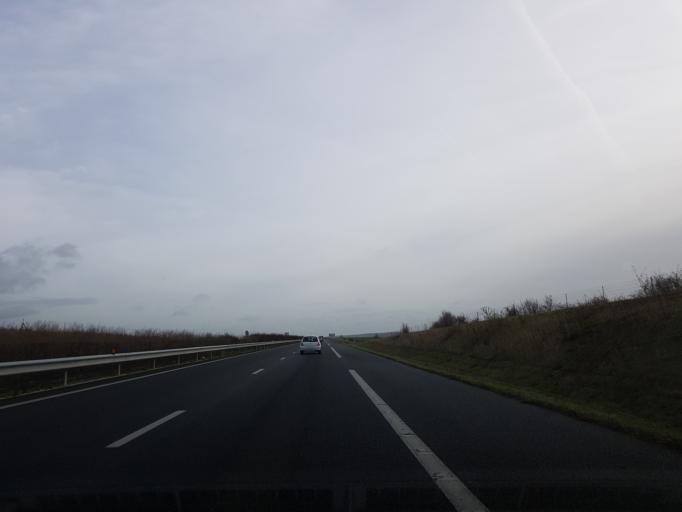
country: FR
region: Champagne-Ardenne
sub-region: Departement de l'Aube
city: Aix-en-Othe
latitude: 48.2431
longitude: 3.5716
